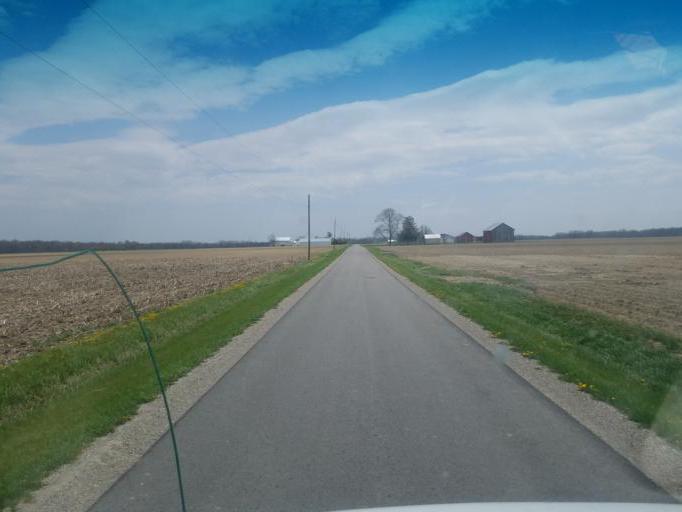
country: US
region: Ohio
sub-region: Wyandot County
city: Upper Sandusky
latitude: 40.7737
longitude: -83.3870
